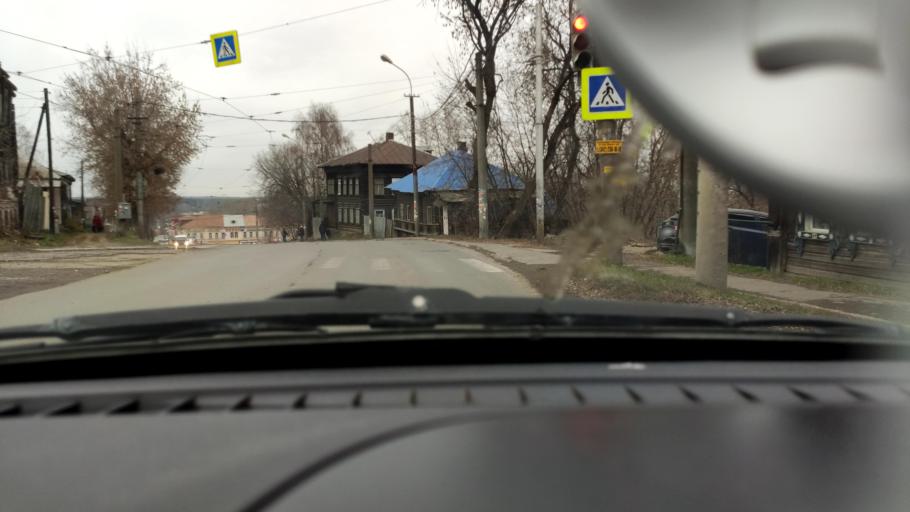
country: RU
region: Perm
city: Perm
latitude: 58.0339
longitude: 56.3128
